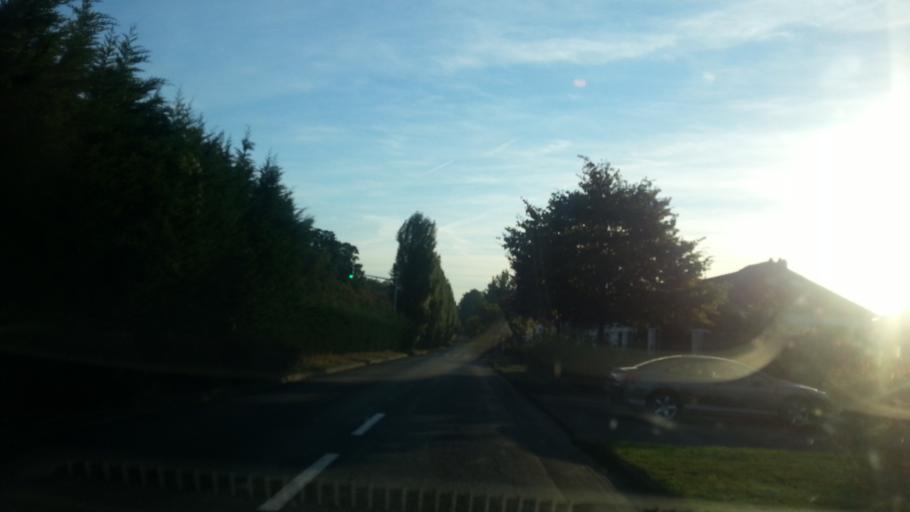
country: FR
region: Picardie
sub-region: Departement de l'Oise
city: Venette
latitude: 49.3997
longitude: 2.8134
